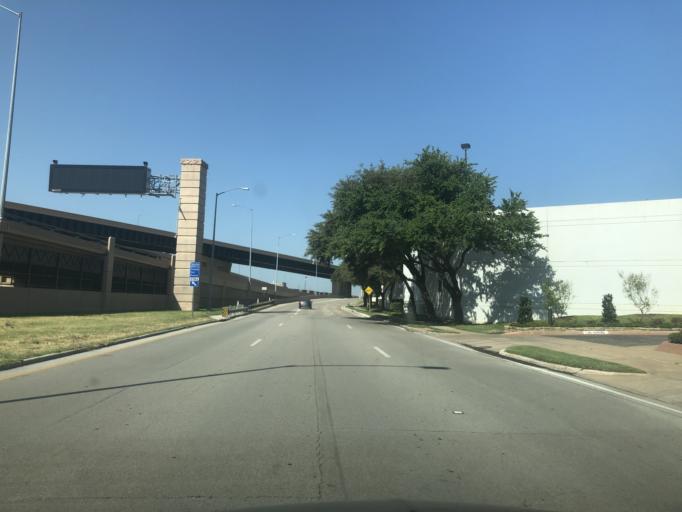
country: US
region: Texas
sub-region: Tarrant County
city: Fort Worth
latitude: 32.7316
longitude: -97.3633
